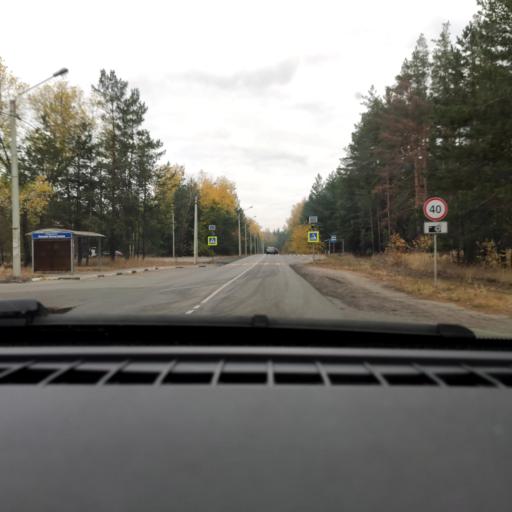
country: RU
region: Voronezj
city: Somovo
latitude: 51.7088
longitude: 39.3259
